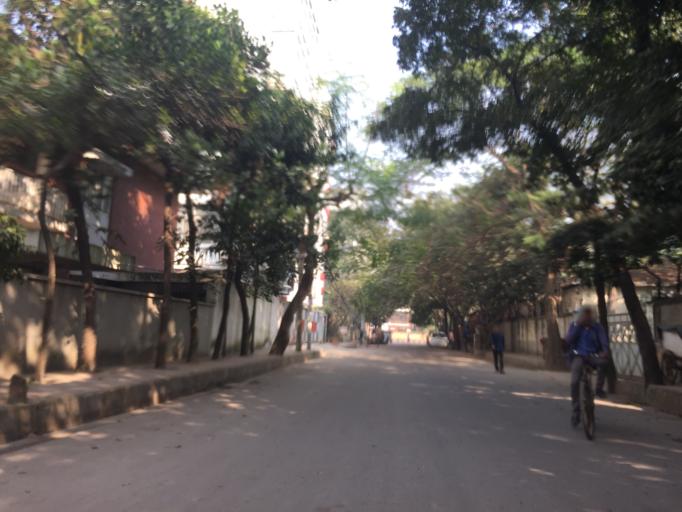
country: BD
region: Dhaka
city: Paltan
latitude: 23.7890
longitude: 90.4091
